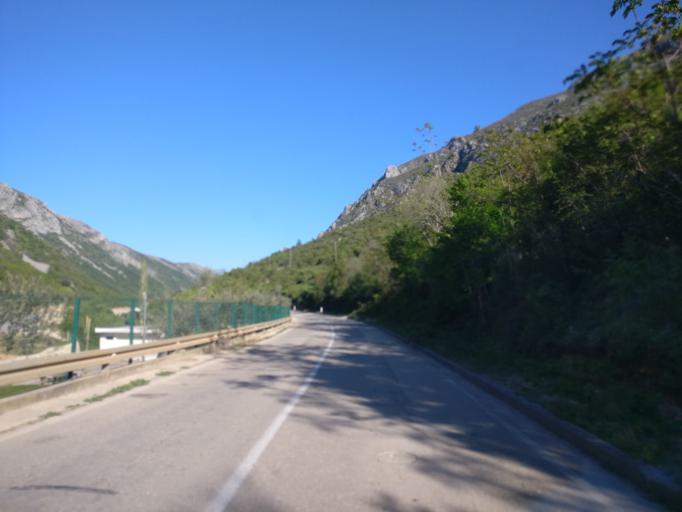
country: BA
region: Federation of Bosnia and Herzegovina
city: Stolac
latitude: 43.0750
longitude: 18.0288
